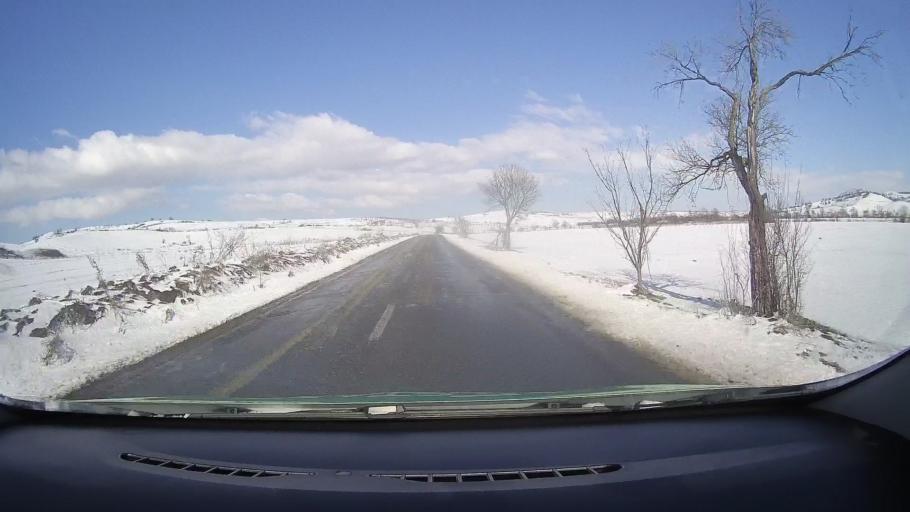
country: RO
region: Sibiu
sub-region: Comuna Vurpar
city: Vurpar
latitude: 45.8673
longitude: 24.3188
